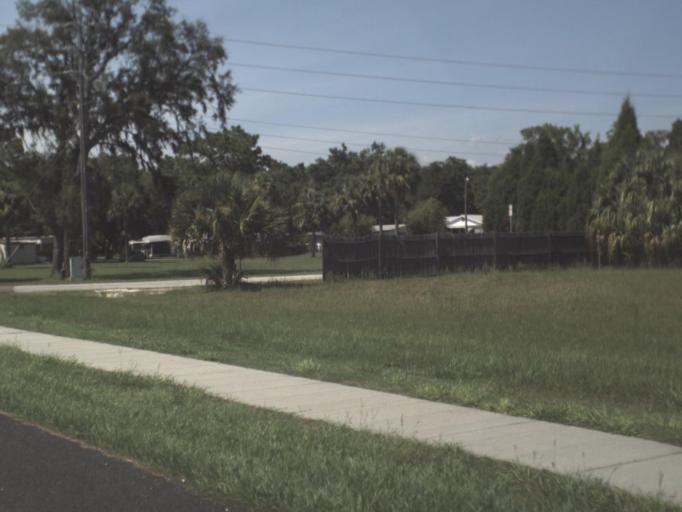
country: US
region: Florida
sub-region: Citrus County
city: Crystal River
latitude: 28.9227
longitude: -82.6118
